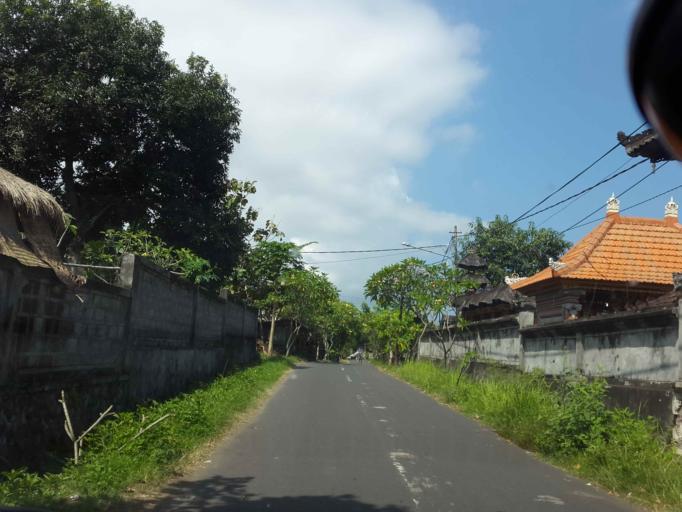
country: ID
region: Bali
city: Klungkung
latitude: -8.5449
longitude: 115.3769
